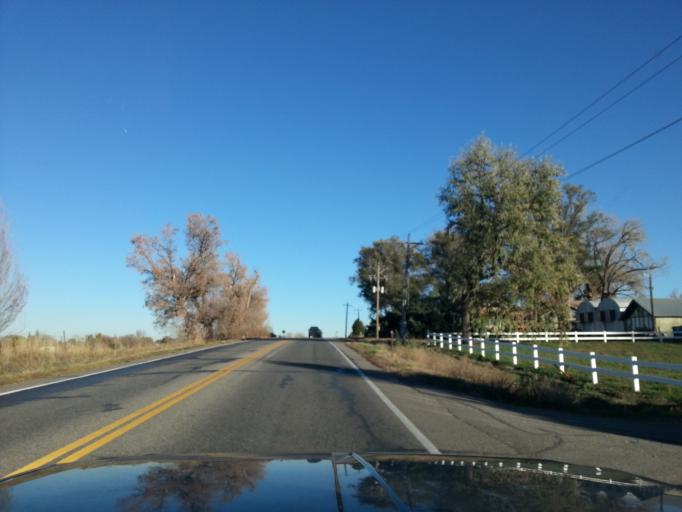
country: US
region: Colorado
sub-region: Larimer County
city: Loveland
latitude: 40.3783
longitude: -105.0179
